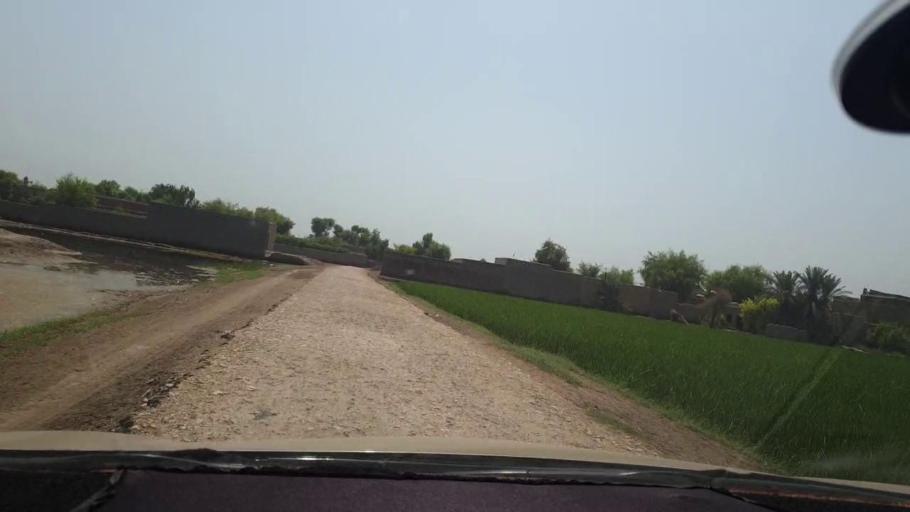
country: PK
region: Sindh
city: Kambar
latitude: 27.6354
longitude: 67.9332
